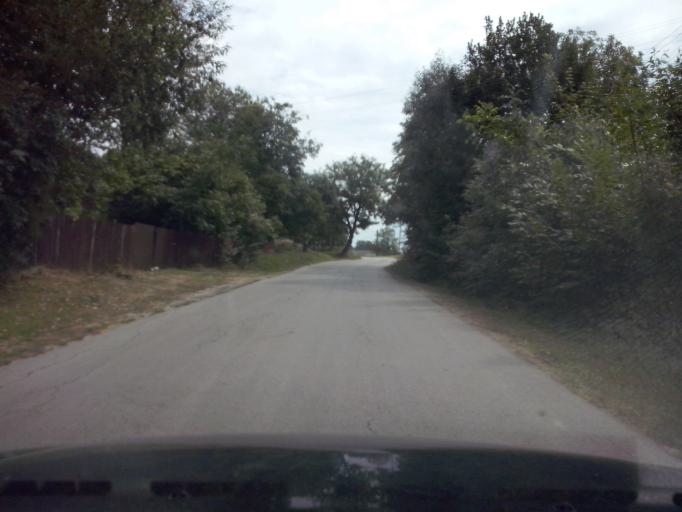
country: PL
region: Swietokrzyskie
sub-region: Powiat kielecki
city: Lagow
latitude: 50.7200
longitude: 21.1169
